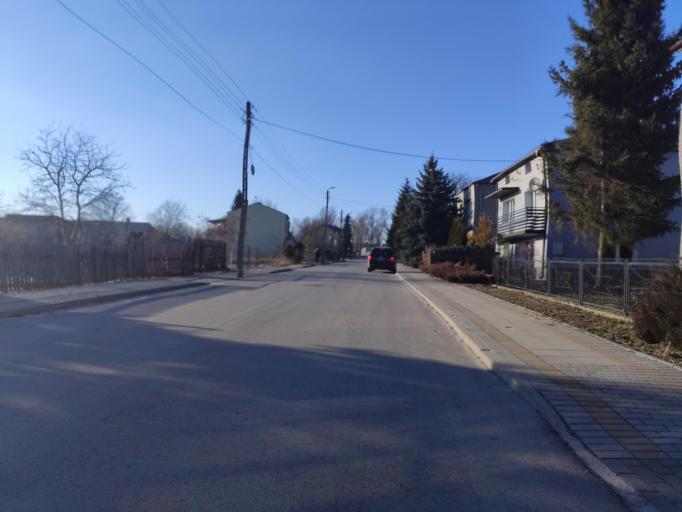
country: PL
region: Lublin Voivodeship
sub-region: Powiat lubartowski
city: Kock
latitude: 51.6422
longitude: 22.4422
